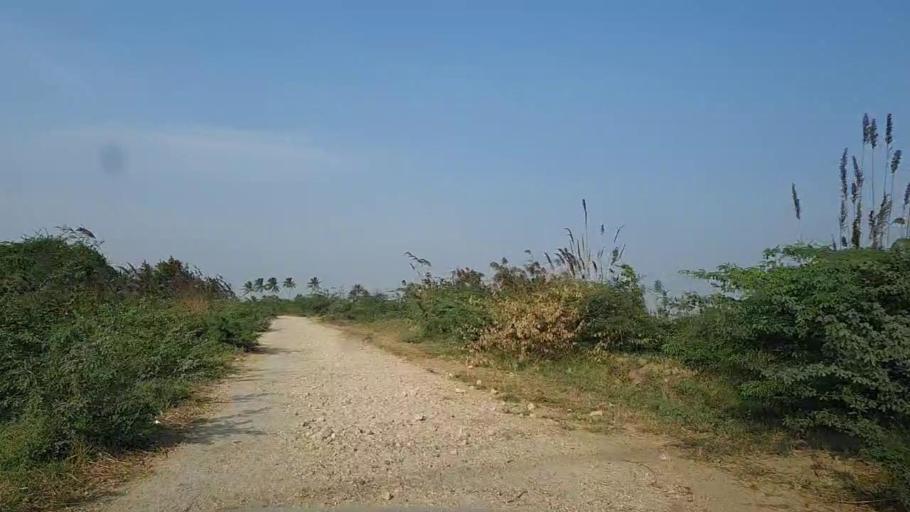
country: PK
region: Sindh
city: Mirpur Sakro
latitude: 24.5876
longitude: 67.6496
